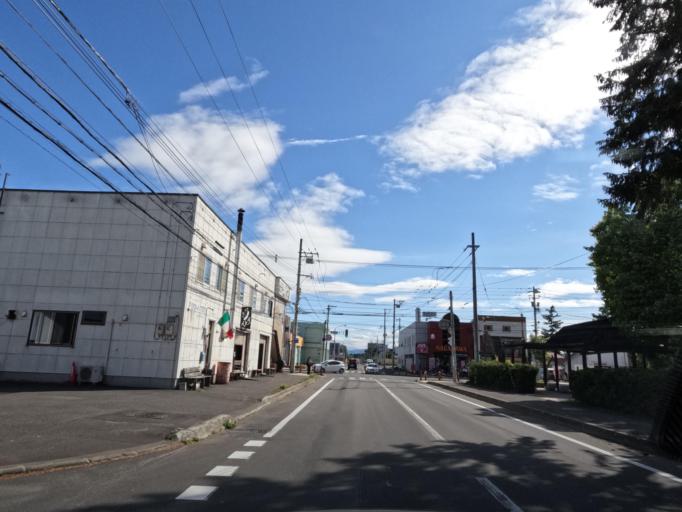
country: JP
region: Hokkaido
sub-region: Asahikawa-shi
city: Asahikawa
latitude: 43.6979
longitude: 142.5081
